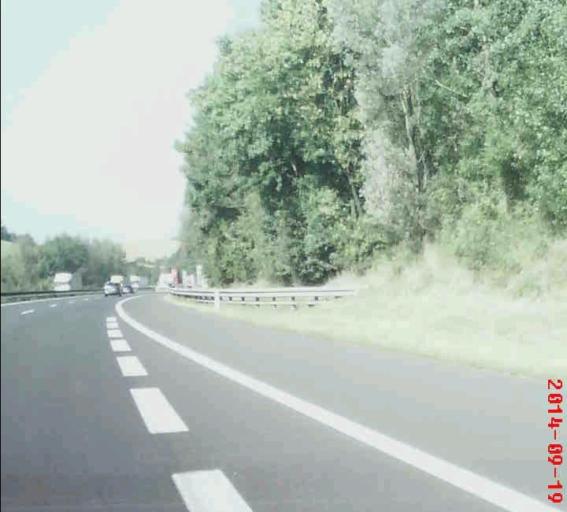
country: AT
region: Upper Austria
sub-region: Wels-Land
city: Gunskirchen
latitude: 48.1855
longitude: 13.9675
